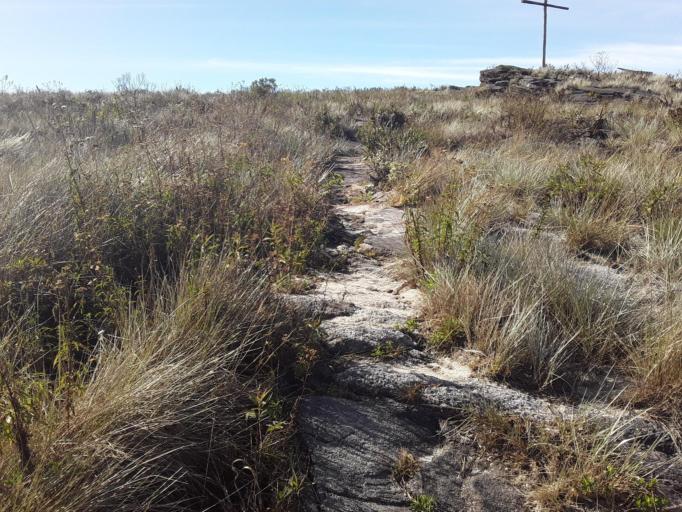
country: BR
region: Minas Gerais
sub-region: Lima Duarte
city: Lima Duarte
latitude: -21.6973
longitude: -43.8983
